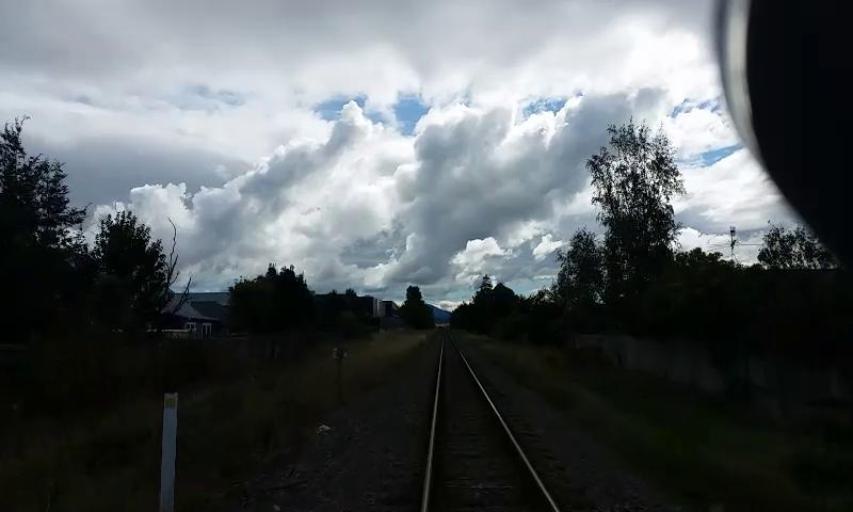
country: NZ
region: Canterbury
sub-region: Waimakariri District
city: Woodend
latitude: -43.3088
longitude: 172.5997
